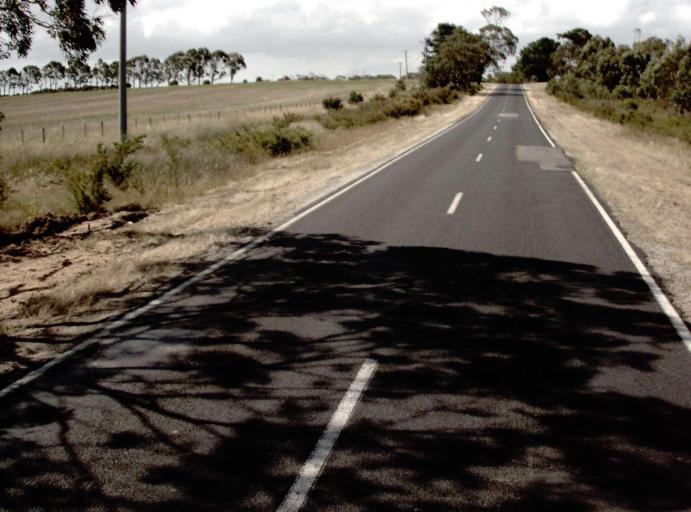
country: AU
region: Victoria
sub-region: Wellington
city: Sale
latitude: -38.3323
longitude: 147.1630
